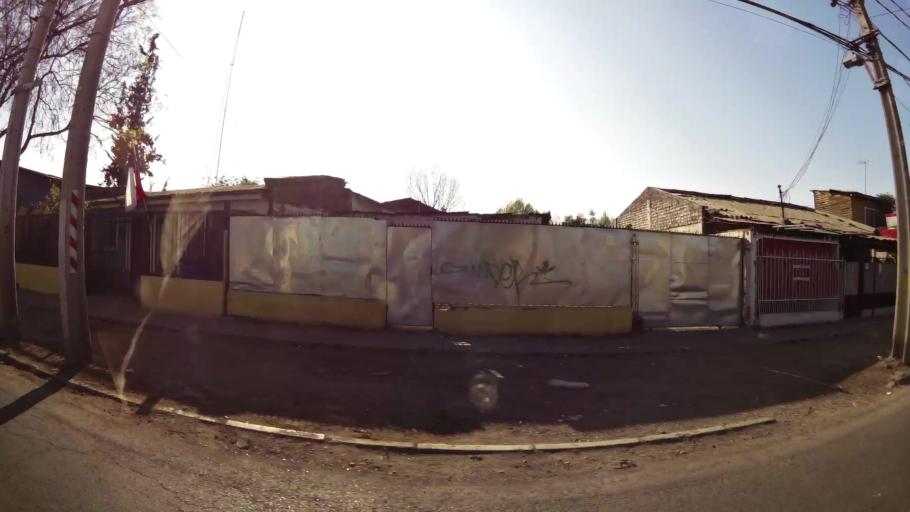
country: CL
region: Santiago Metropolitan
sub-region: Provincia de Santiago
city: Santiago
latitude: -33.3927
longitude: -70.6572
